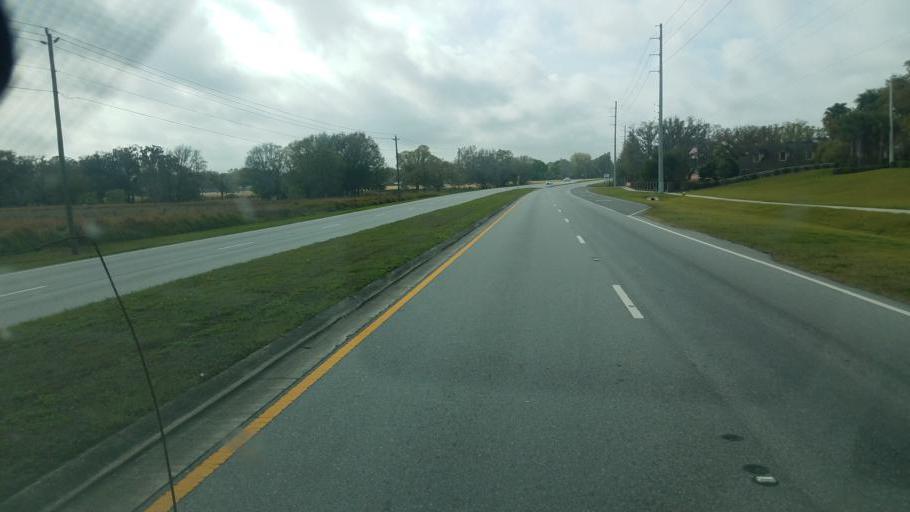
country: US
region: Florida
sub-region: Polk County
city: Winston
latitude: 27.9948
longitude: -82.0558
